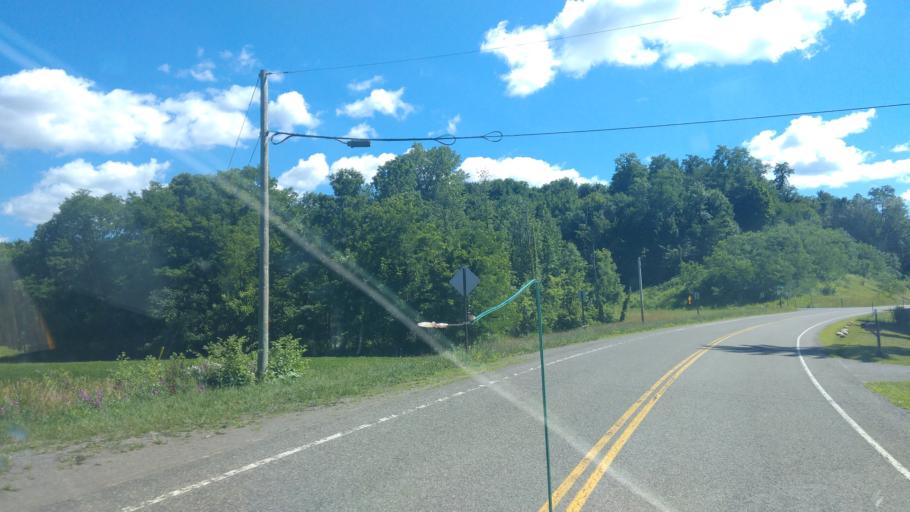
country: US
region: New York
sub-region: Wayne County
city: Sodus
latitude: 43.1762
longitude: -77.0108
